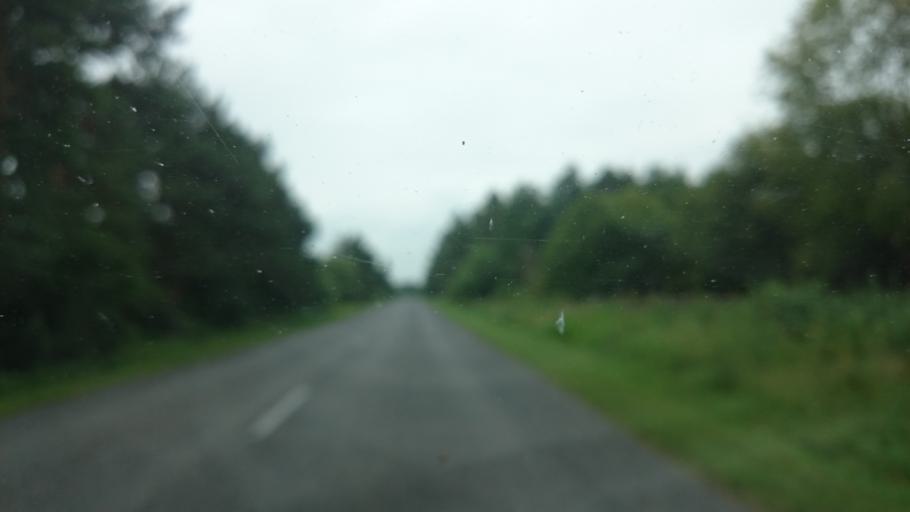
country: EE
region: Saare
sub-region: Orissaare vald
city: Orissaare
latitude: 58.5786
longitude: 23.0280
